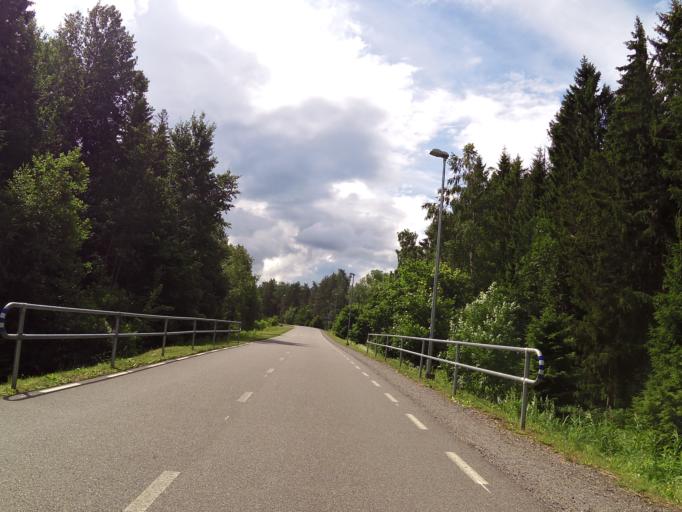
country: EE
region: Harju
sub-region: Saue vald
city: Laagri
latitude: 59.3908
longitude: 24.6254
